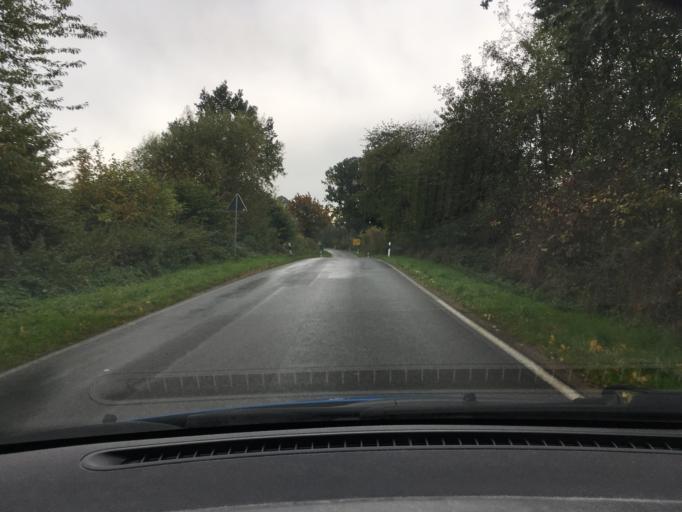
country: DE
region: Schleswig-Holstein
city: Bosau
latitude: 54.0877
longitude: 10.4272
